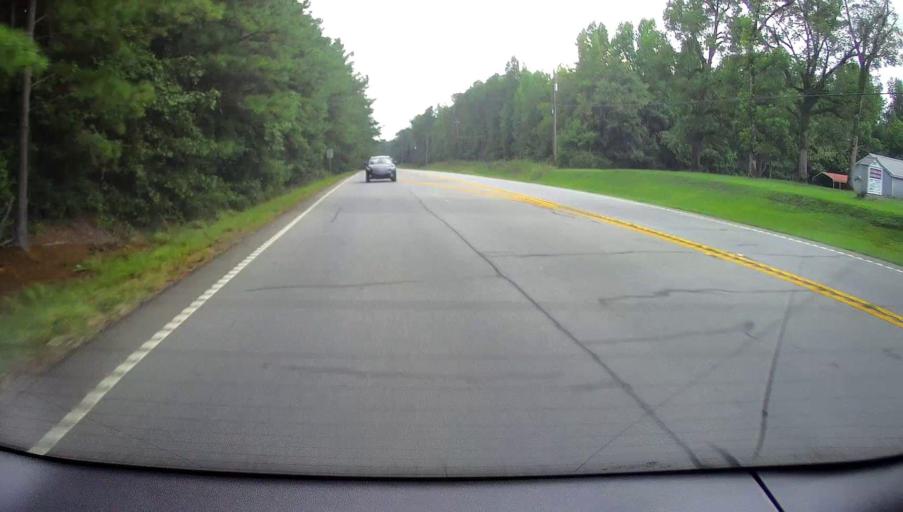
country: US
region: Georgia
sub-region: Coweta County
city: Senoia
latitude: 33.1871
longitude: -84.5805
